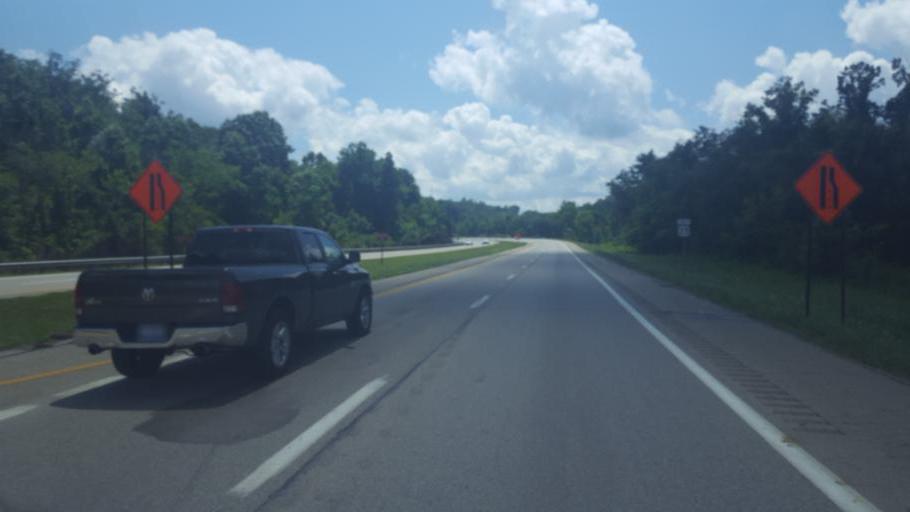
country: US
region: Ohio
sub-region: Jackson County
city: Jackson
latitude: 39.1264
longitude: -82.7014
